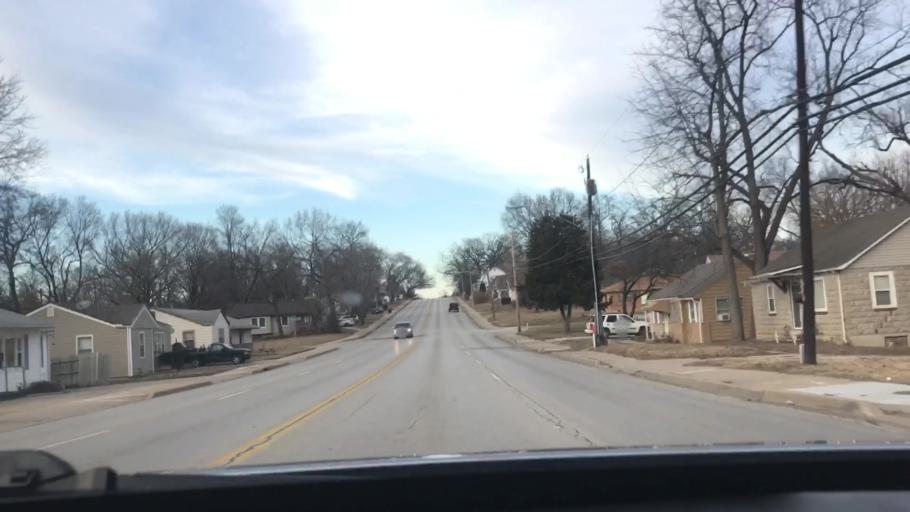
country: US
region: Missouri
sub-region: Jackson County
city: Independence
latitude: 39.0747
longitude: -94.4463
